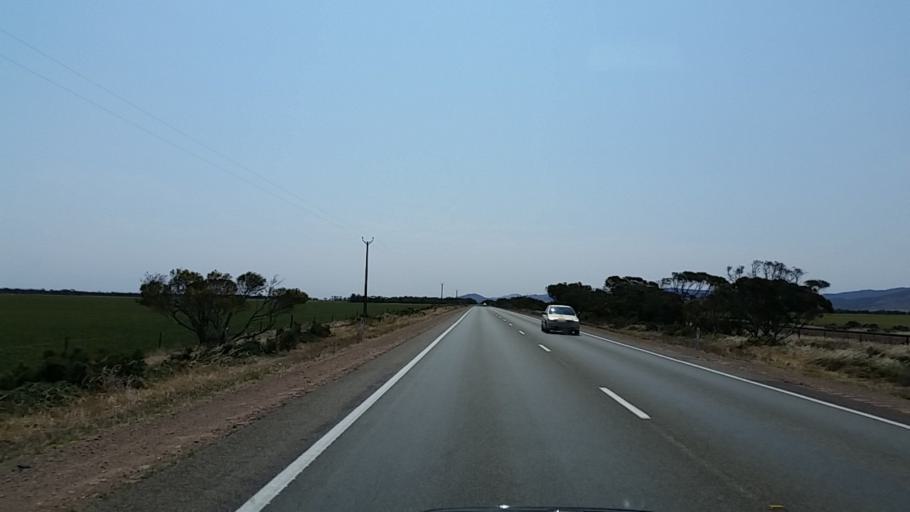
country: AU
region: South Australia
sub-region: Port Pirie City and Dists
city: Port Pirie
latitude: -32.9554
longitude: 137.9825
